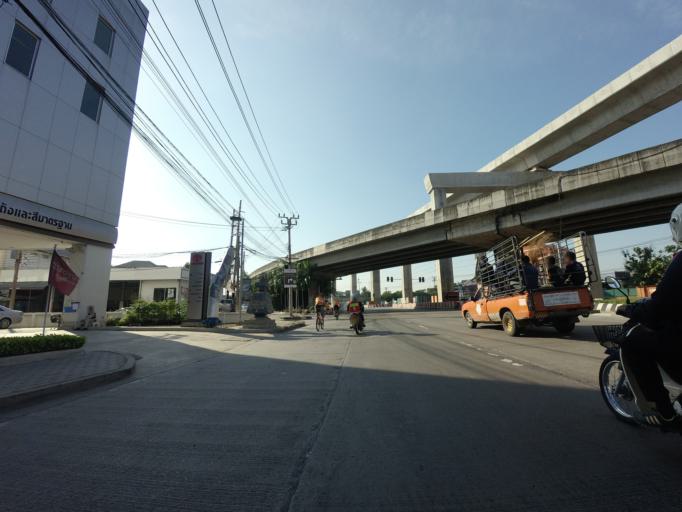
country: TH
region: Samut Prakan
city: Samut Prakan
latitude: 13.6277
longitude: 100.5884
